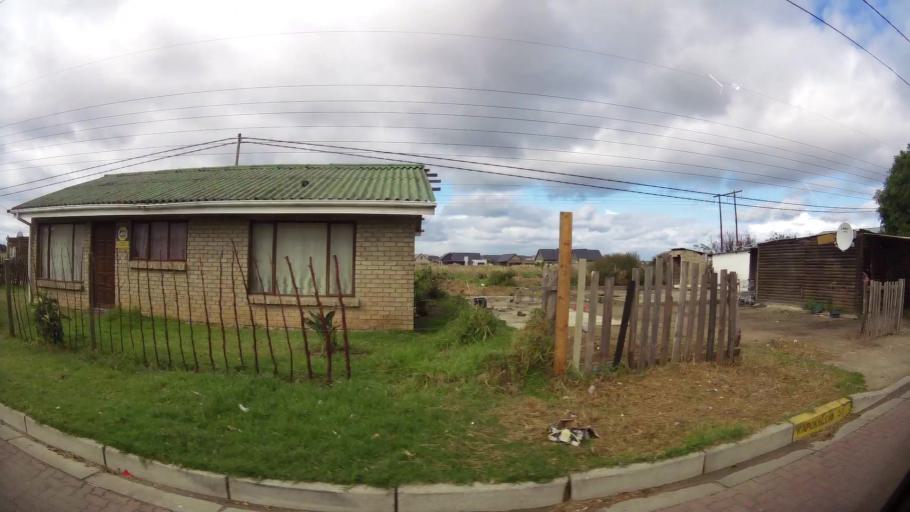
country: ZA
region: Western Cape
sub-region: Eden District Municipality
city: George
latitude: -33.9795
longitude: 22.4910
